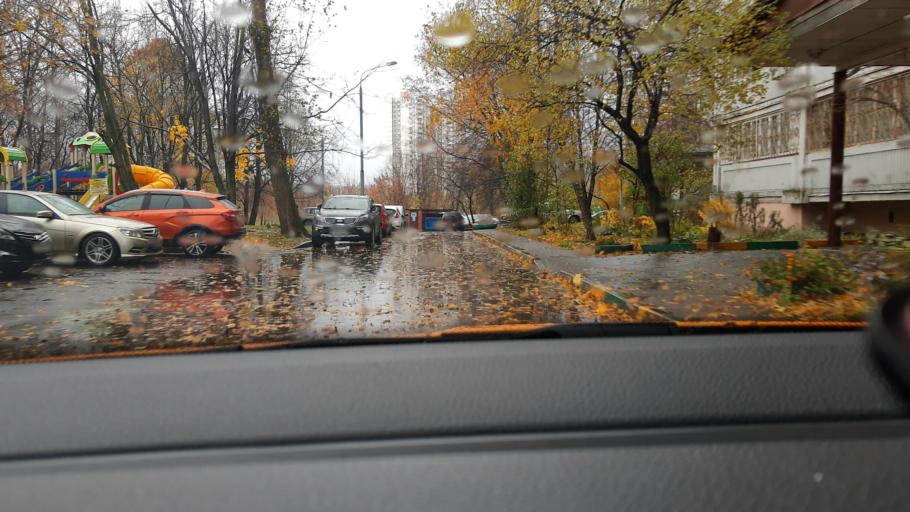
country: RU
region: Moscow
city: Nikulino
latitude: 55.6762
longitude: 37.4566
